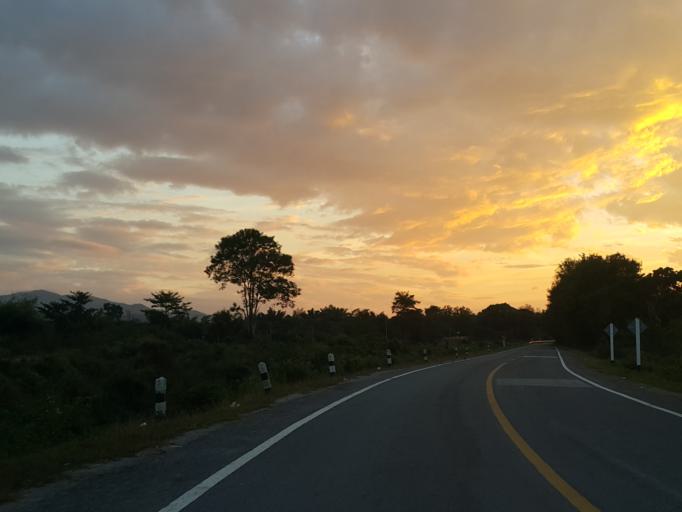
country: TH
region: Lampang
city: Mae Mo
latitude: 18.3820
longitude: 99.6097
